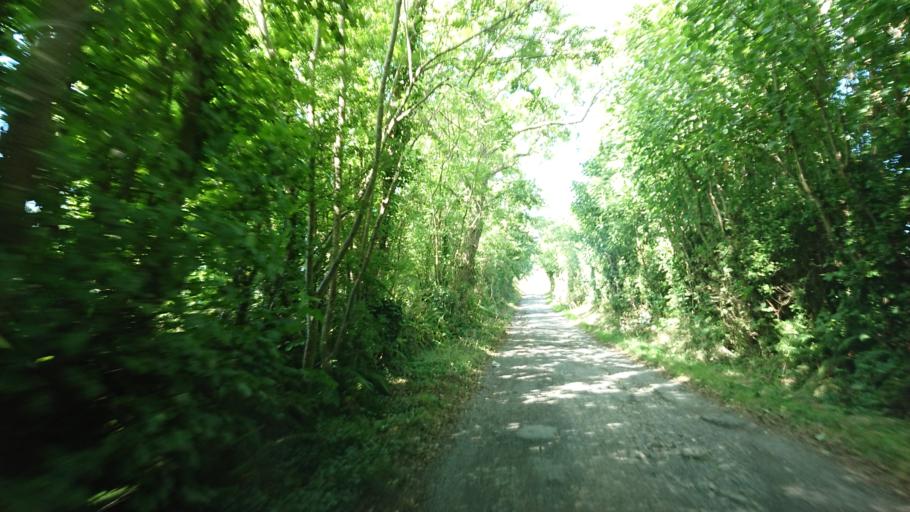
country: IE
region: Munster
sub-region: Waterford
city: Waterford
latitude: 52.2297
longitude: -7.1514
